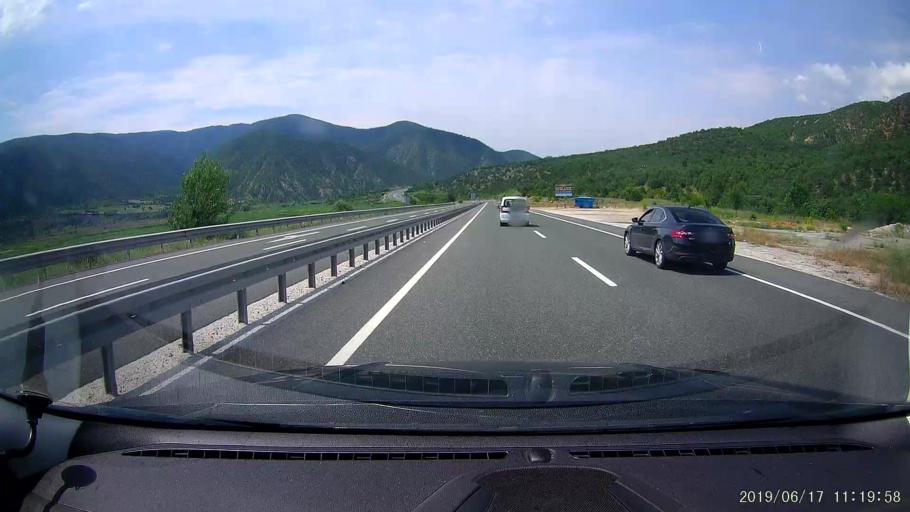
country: TR
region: Cankiri
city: Yaprakli
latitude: 40.9192
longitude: 33.8155
